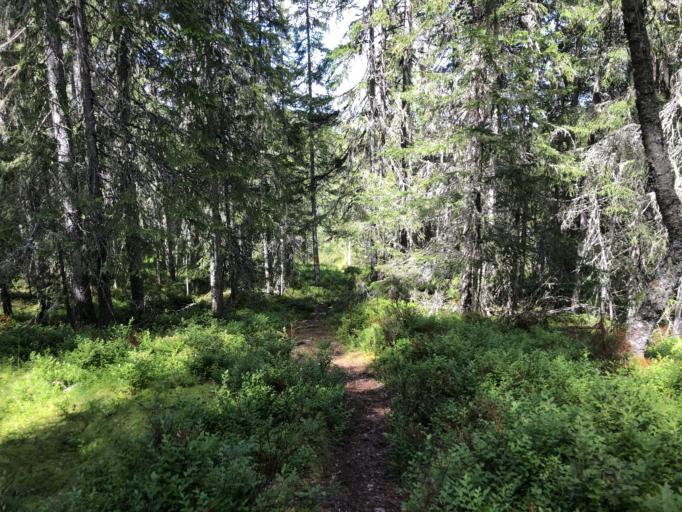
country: SE
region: Dalarna
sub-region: Vansbro Kommun
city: Jarna
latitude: 60.6688
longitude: 14.2705
